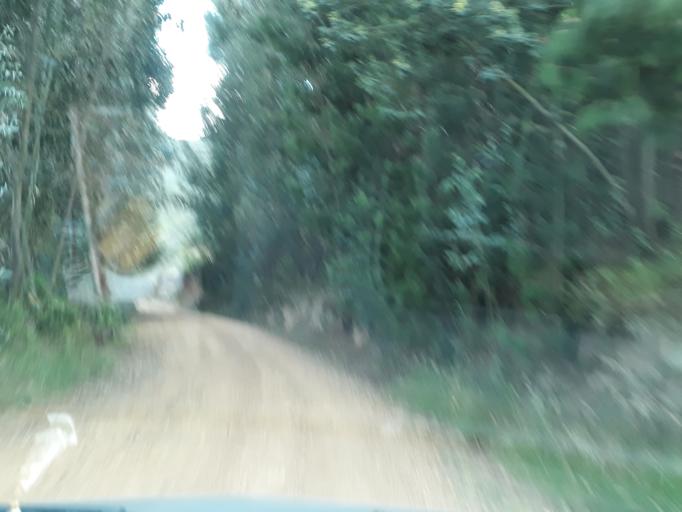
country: CO
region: Boyaca
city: Santa Rosa de Viterbo
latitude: 5.8631
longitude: -72.9686
